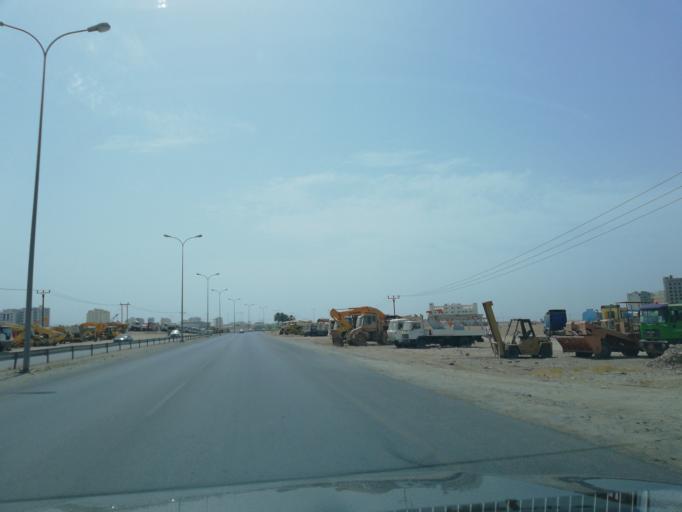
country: OM
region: Muhafazat Masqat
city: Bawshar
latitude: 23.5829
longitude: 58.3637
